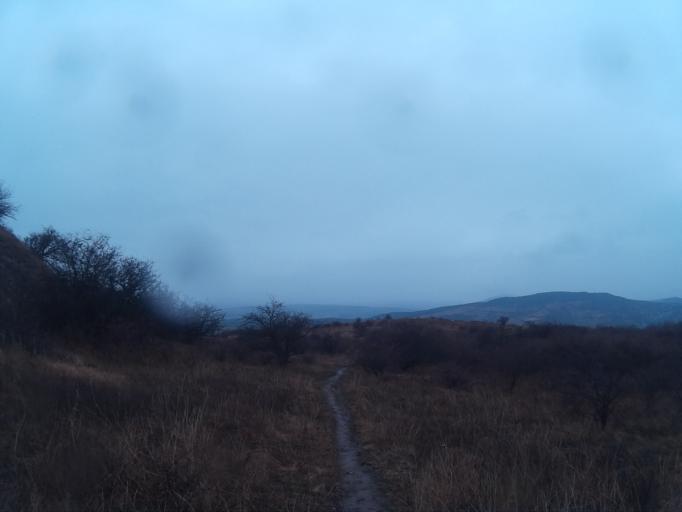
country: HU
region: Komarom-Esztergom
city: Tokod
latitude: 47.7141
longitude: 18.6406
